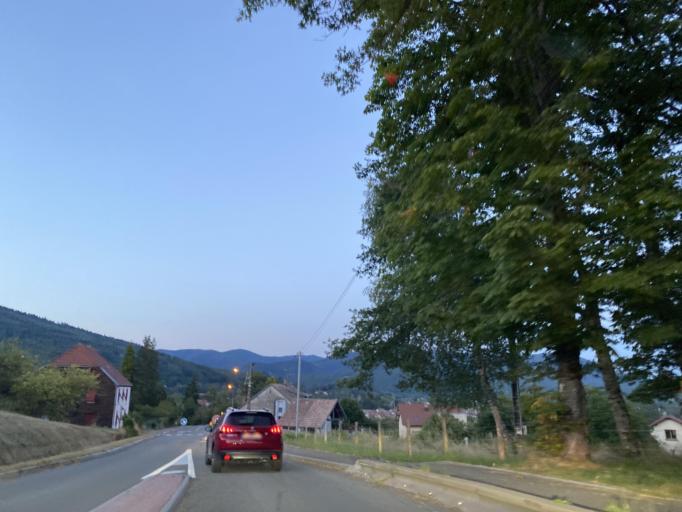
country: FR
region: Franche-Comte
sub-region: Territoire de Belfort
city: Giromagny
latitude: 47.7408
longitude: 6.8160
